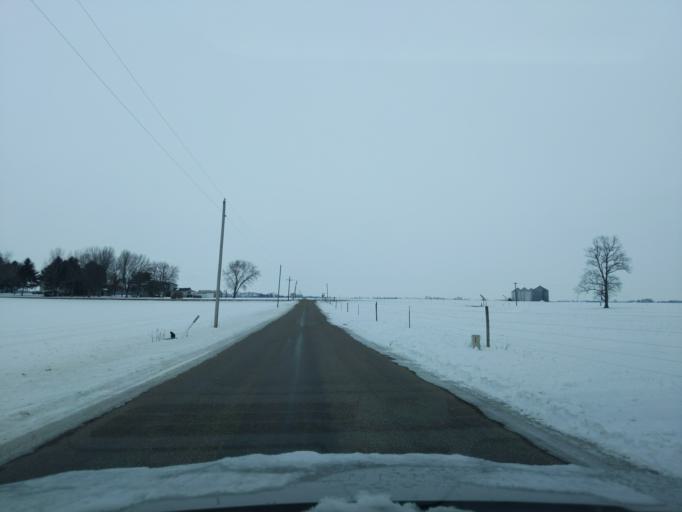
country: US
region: Indiana
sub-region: Benton County
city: Otterbein
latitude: 40.4445
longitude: -87.0926
